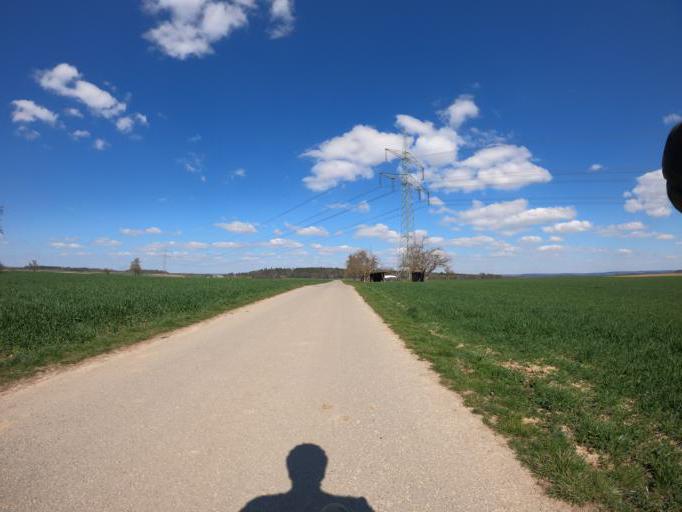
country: DE
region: Baden-Wuerttemberg
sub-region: Regierungsbezirk Stuttgart
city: Bondorf
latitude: 48.4723
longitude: 8.8670
